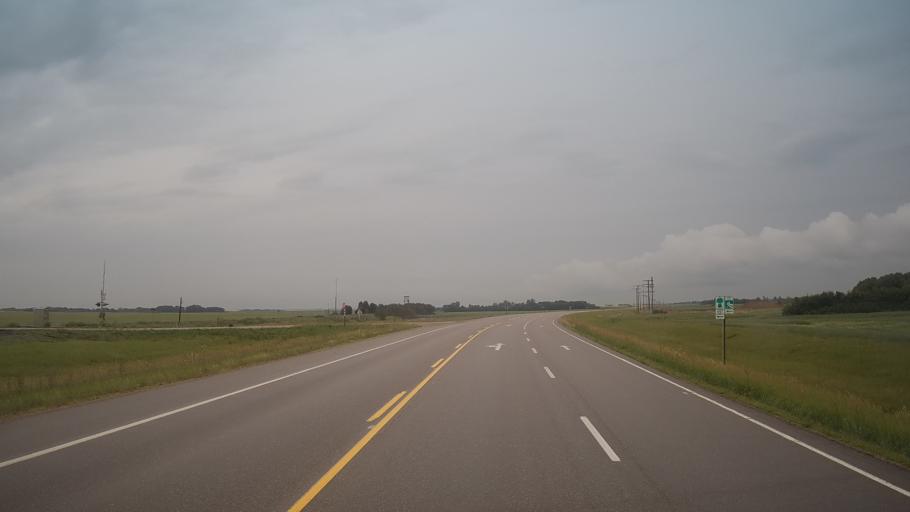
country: CA
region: Saskatchewan
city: Wilkie
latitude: 52.3111
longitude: -108.6919
